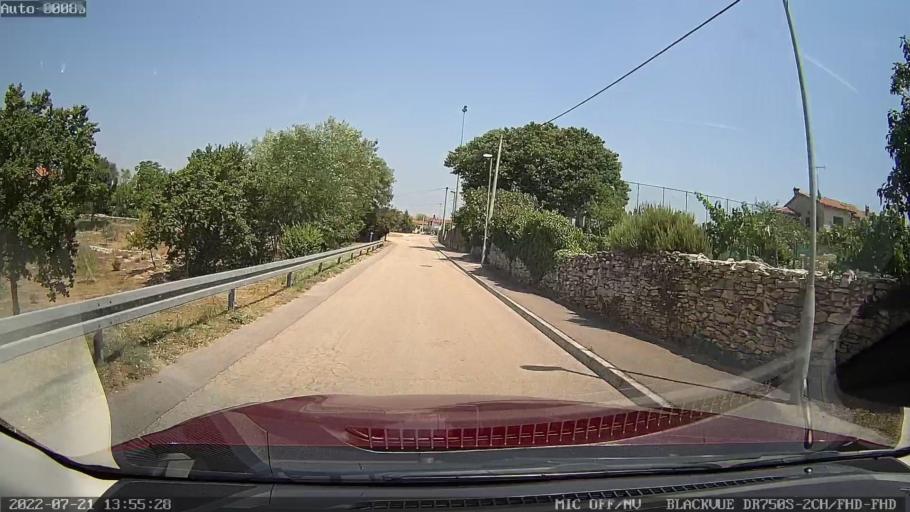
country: HR
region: Istarska
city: Pazin
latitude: 45.1213
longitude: 13.8373
